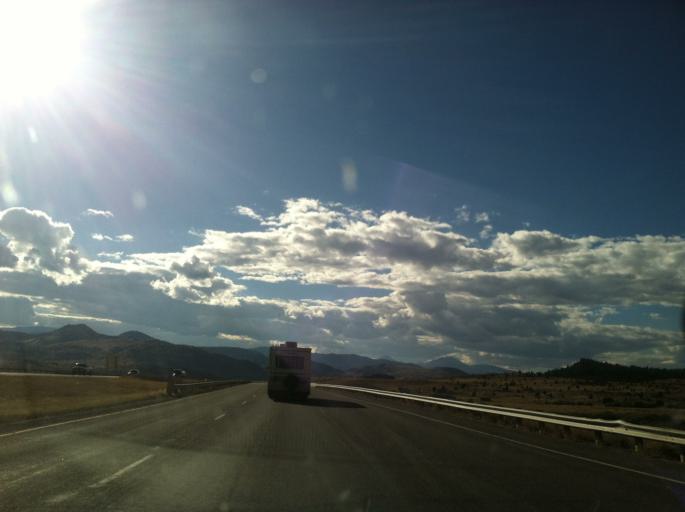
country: US
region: Montana
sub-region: Silver Bow County
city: Butte-Silver Bow (Balance)
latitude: 46.0102
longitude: -112.6895
